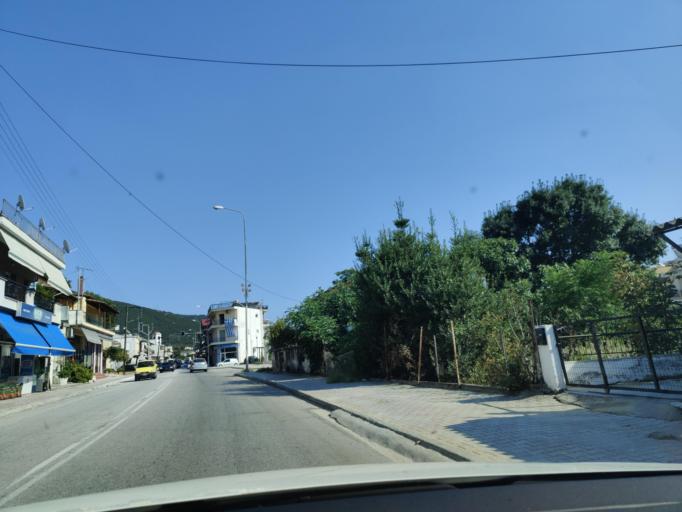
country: GR
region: East Macedonia and Thrace
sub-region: Nomos Kavalas
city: Amygdaleonas
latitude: 40.9646
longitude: 24.3569
